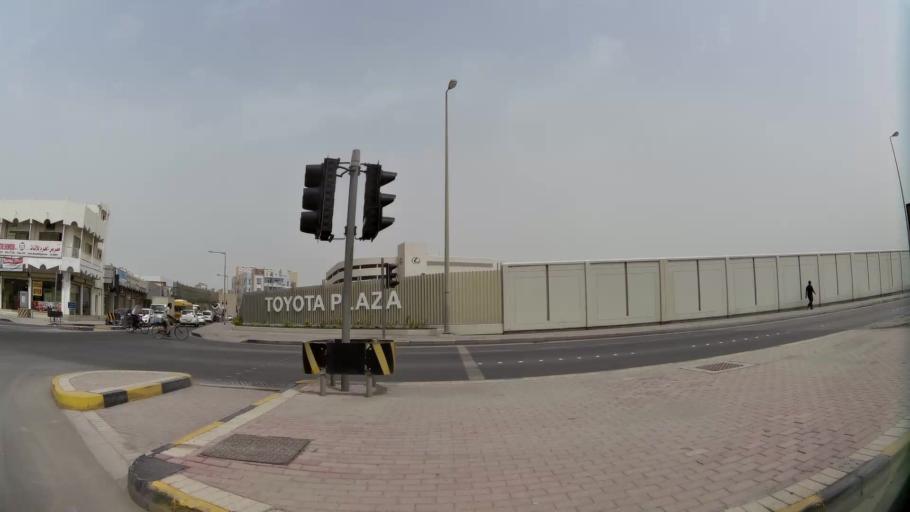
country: BH
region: Northern
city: Madinat `Isa
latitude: 26.1868
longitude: 50.5396
